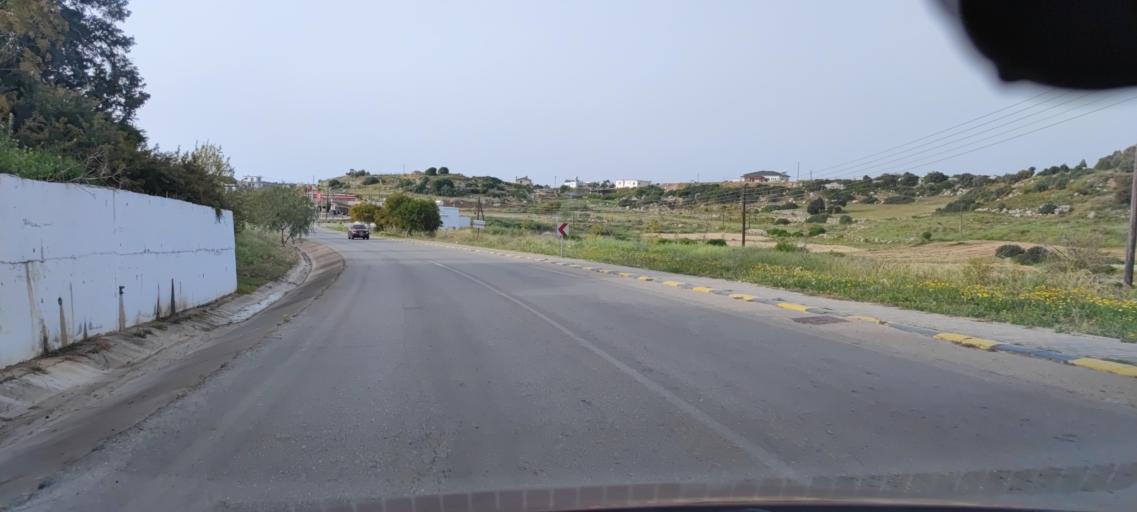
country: CY
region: Ammochostos
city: Leonarisso
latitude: 35.5039
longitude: 34.1615
